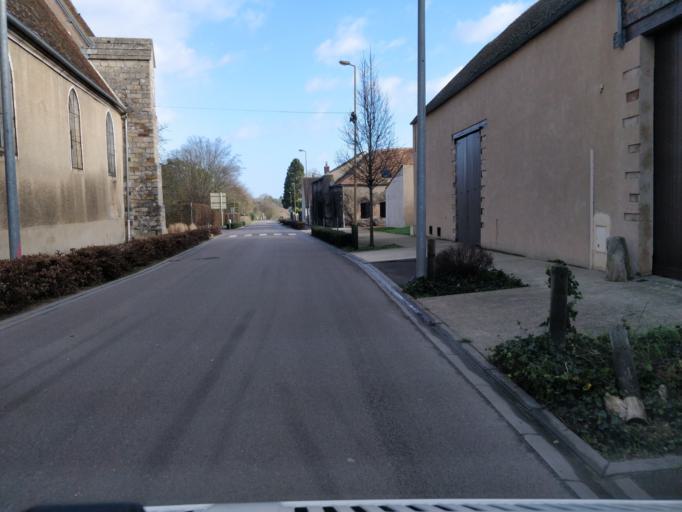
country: FR
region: Bourgogne
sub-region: Departement de l'Yonne
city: Cheroy
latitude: 48.2025
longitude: 2.9999
